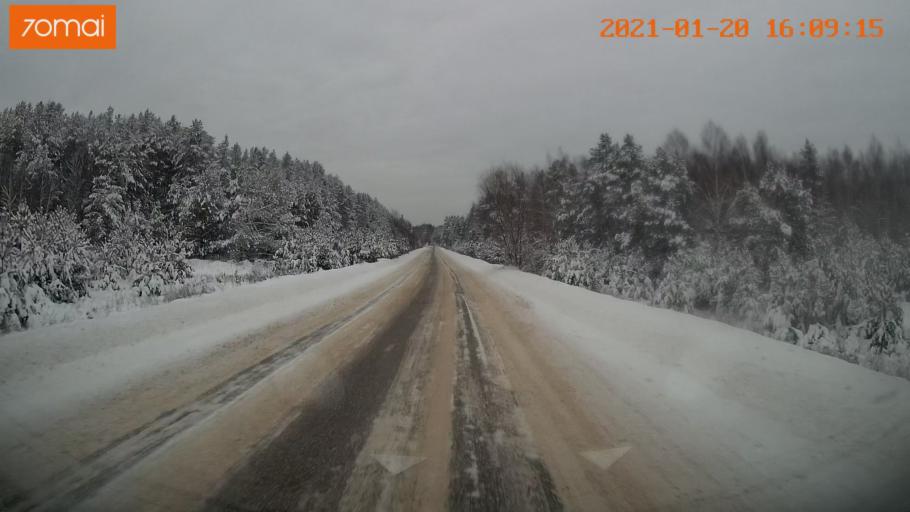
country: RU
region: Vladimir
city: Sudogda
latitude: 56.0803
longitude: 40.7755
